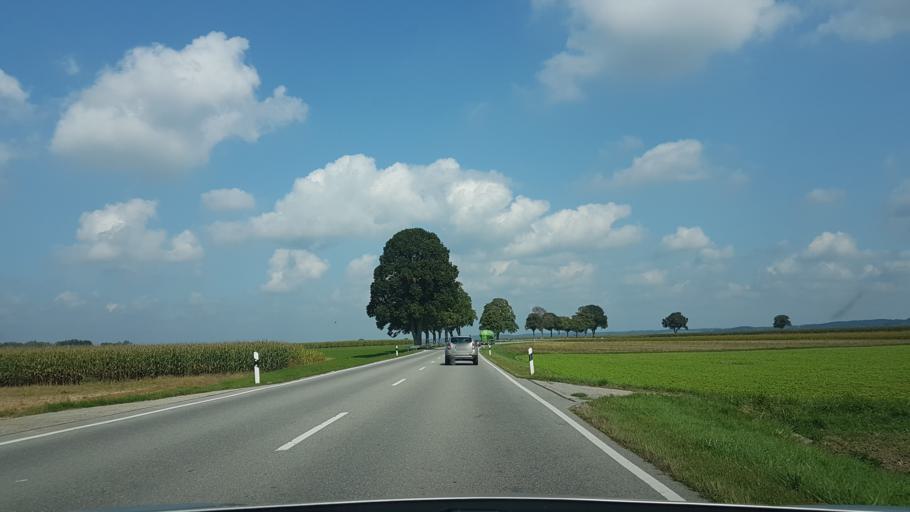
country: DE
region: Bavaria
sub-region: Upper Bavaria
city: Bockhorn
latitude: 48.3149
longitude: 11.9498
